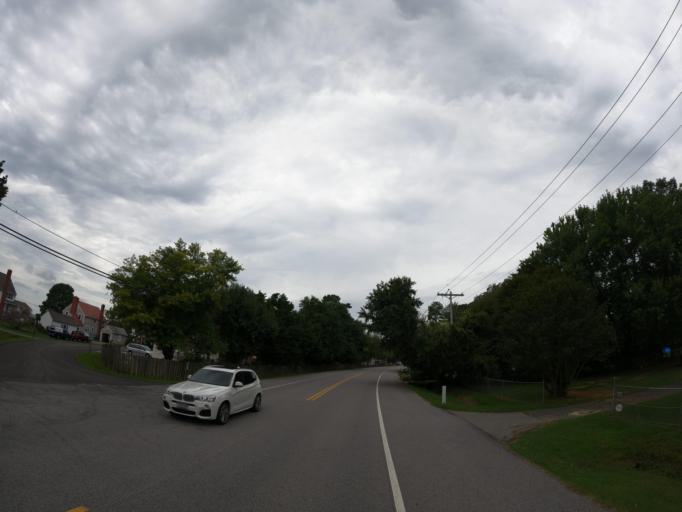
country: US
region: Maryland
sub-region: Saint Mary's County
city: Lexington Park
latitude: 38.1410
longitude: -76.5059
